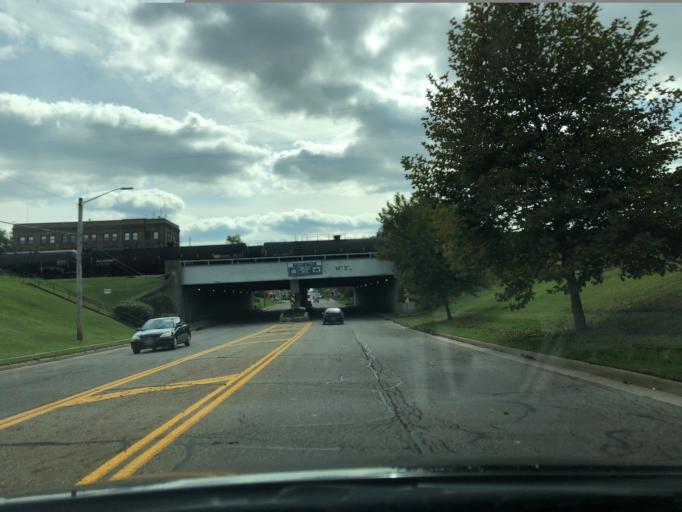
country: US
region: Ohio
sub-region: Stark County
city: Brewster
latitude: 40.7149
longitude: -81.5976
